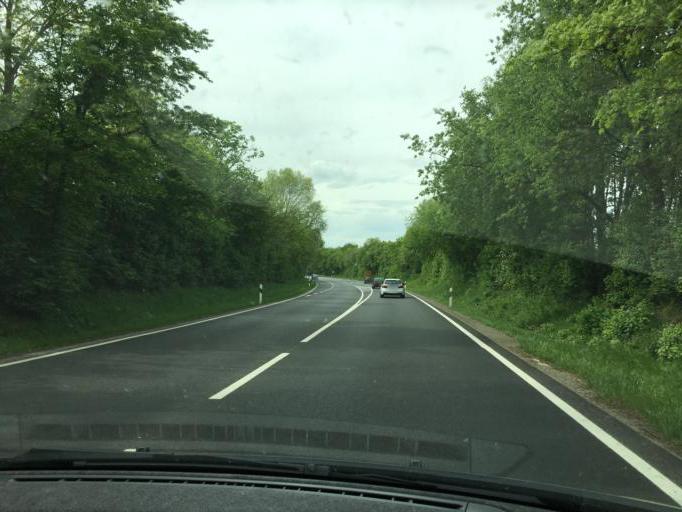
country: DE
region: North Rhine-Westphalia
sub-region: Regierungsbezirk Koln
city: Euskirchen
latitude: 50.6869
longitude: 6.7448
